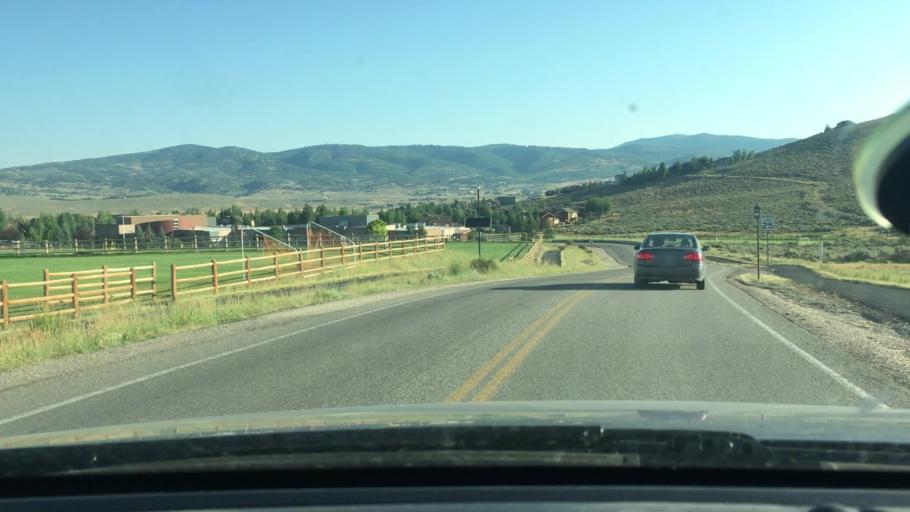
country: US
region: Utah
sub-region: Summit County
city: Snyderville
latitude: 40.7125
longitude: -111.5017
